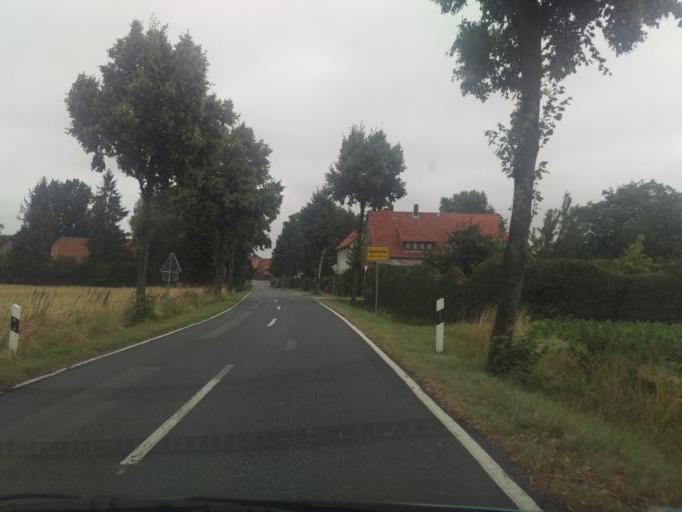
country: DE
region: Lower Saxony
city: Schellerten
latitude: 52.1807
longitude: 10.1012
